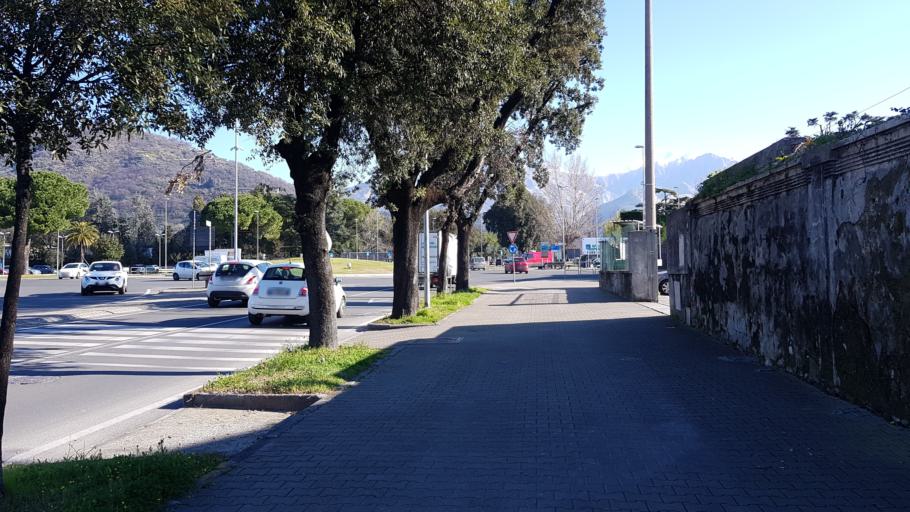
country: IT
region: Tuscany
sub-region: Provincia di Massa-Carrara
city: Carrara
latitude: 44.0545
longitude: 10.0626
